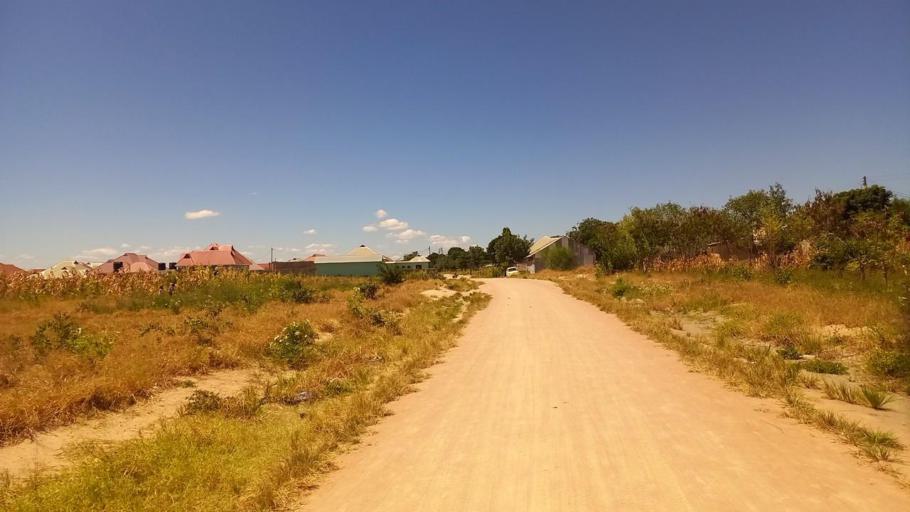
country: TZ
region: Dodoma
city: Dodoma
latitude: -6.1302
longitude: 35.7343
